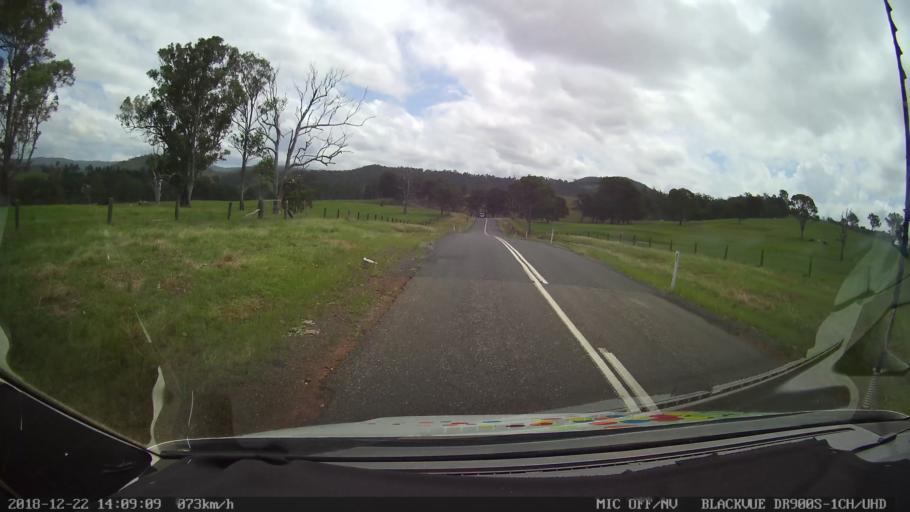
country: AU
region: New South Wales
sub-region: Clarence Valley
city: Coutts Crossing
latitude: -29.9844
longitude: 152.7200
